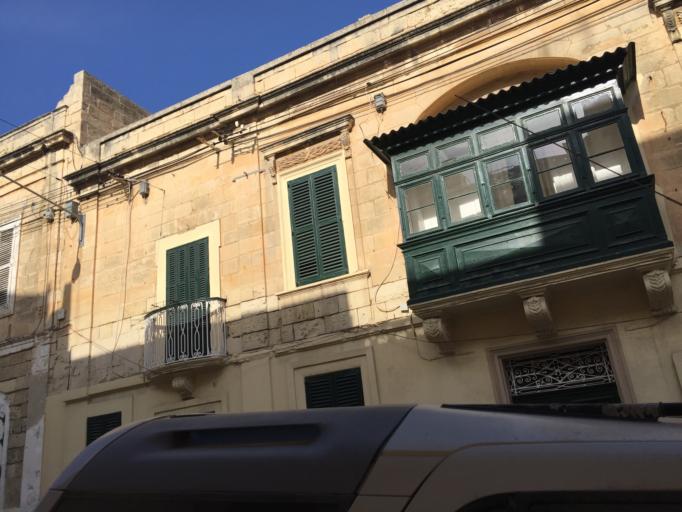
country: MT
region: Tas-Sliema
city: Sliema
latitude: 35.9107
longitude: 14.5014
